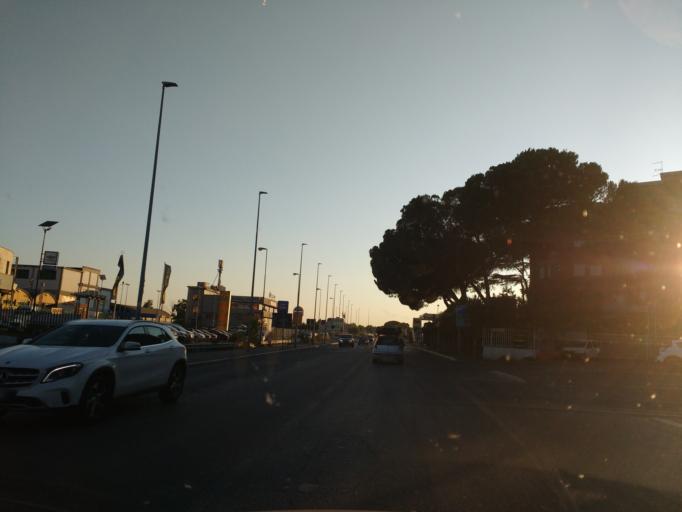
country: IT
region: Latium
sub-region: Citta metropolitana di Roma Capitale
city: Villanova
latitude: 41.9565
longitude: 12.7563
